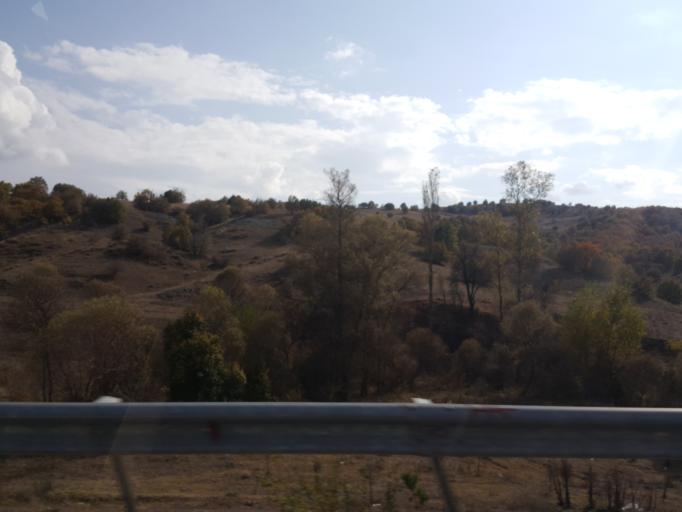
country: TR
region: Corum
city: Alaca
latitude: 40.3176
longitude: 34.6805
